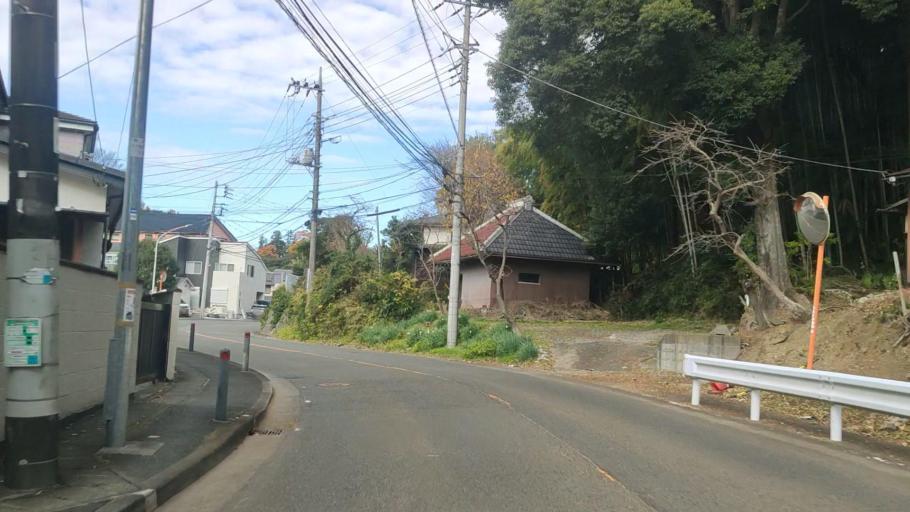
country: JP
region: Kanagawa
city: Yokohama
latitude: 35.4374
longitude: 139.5445
